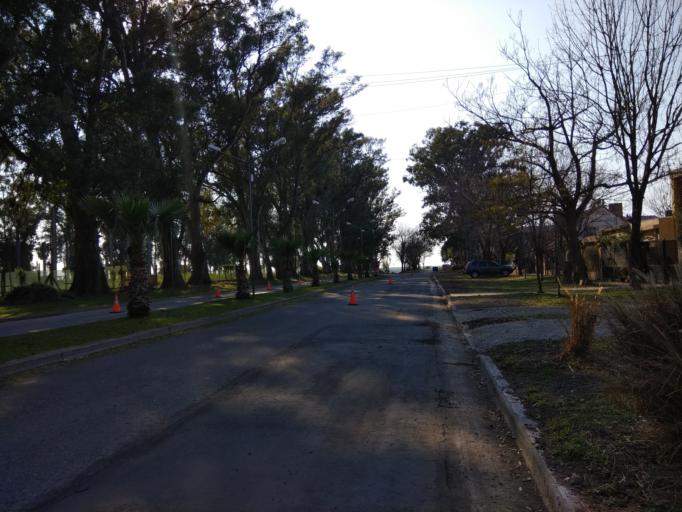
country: AR
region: Santa Fe
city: Granadero Baigorria
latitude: -32.8473
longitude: -60.6994
